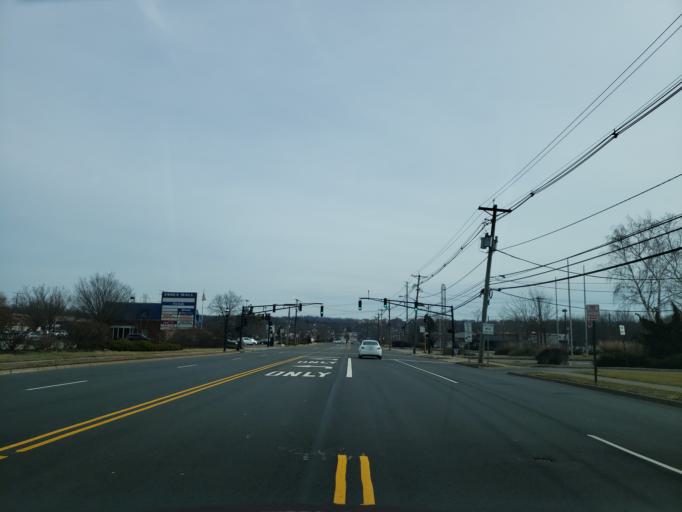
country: US
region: New Jersey
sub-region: Essex County
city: Westville
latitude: 40.8526
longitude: -74.3022
